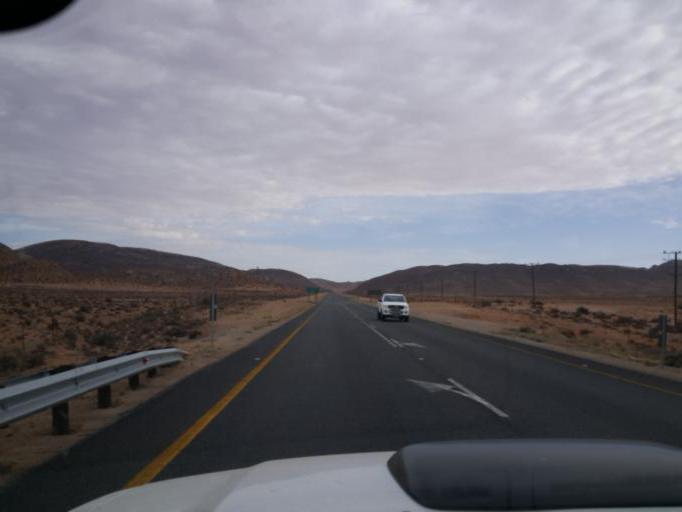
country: ZA
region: Northern Cape
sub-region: Namakwa District Municipality
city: Springbok
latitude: -29.4718
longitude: 17.8374
